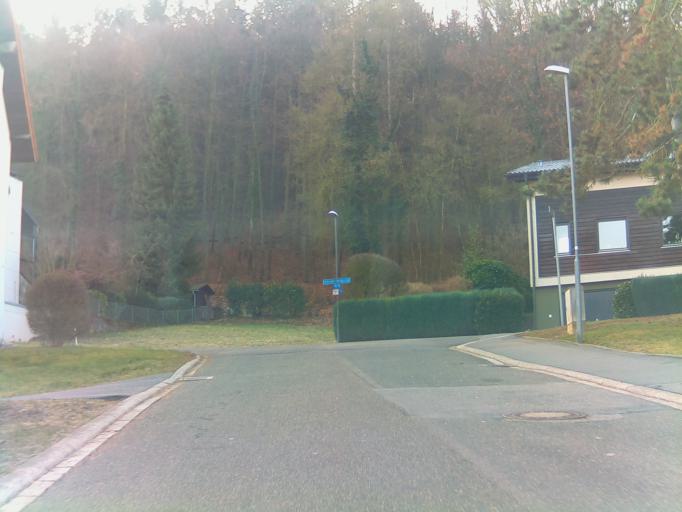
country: DE
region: Baden-Wuerttemberg
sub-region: Karlsruhe Region
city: Mosbach
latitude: 49.3425
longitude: 9.1332
